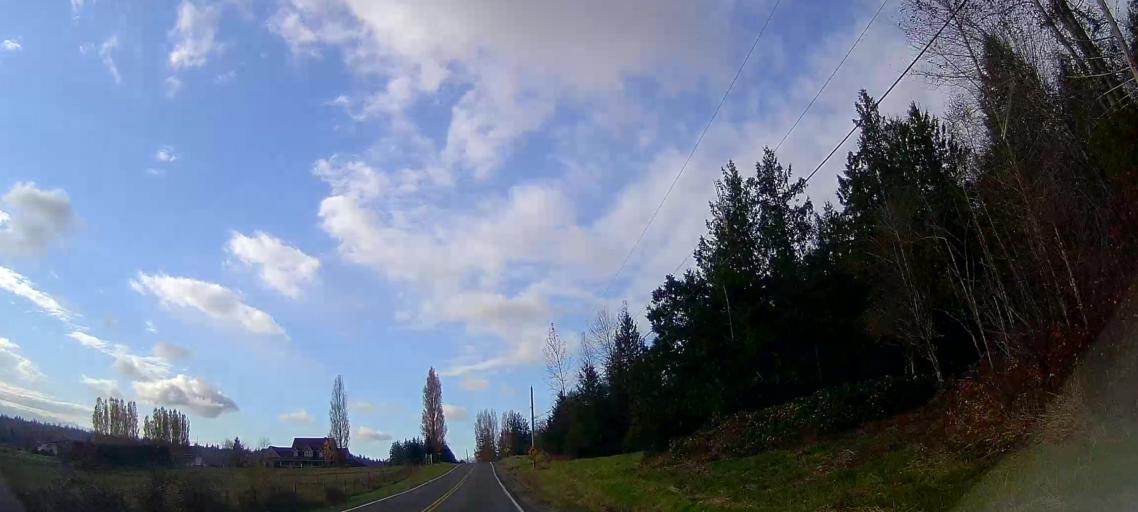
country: US
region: Washington
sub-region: Skagit County
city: Big Lake
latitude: 48.4170
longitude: -122.2305
